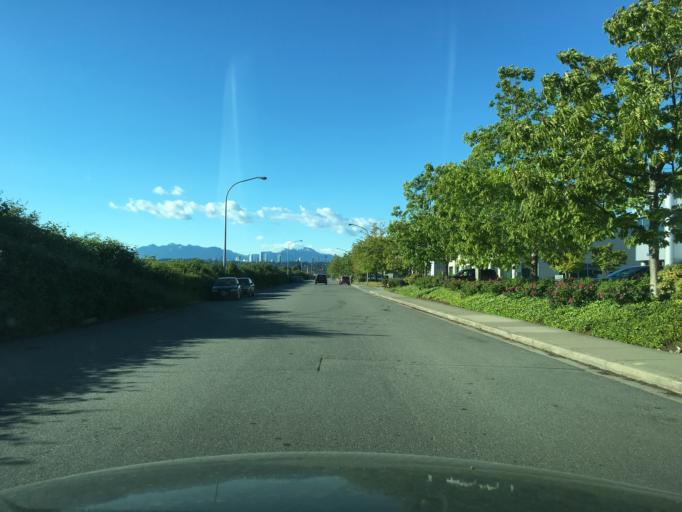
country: CA
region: British Columbia
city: Delta
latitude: 49.1645
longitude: -122.9940
